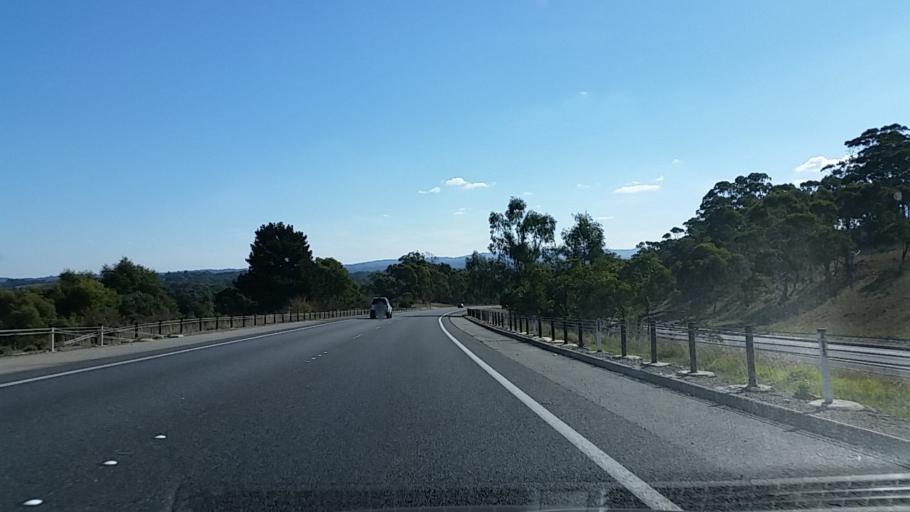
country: AU
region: South Australia
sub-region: Mount Barker
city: Hahndorf
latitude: -35.0487
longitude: 138.8238
